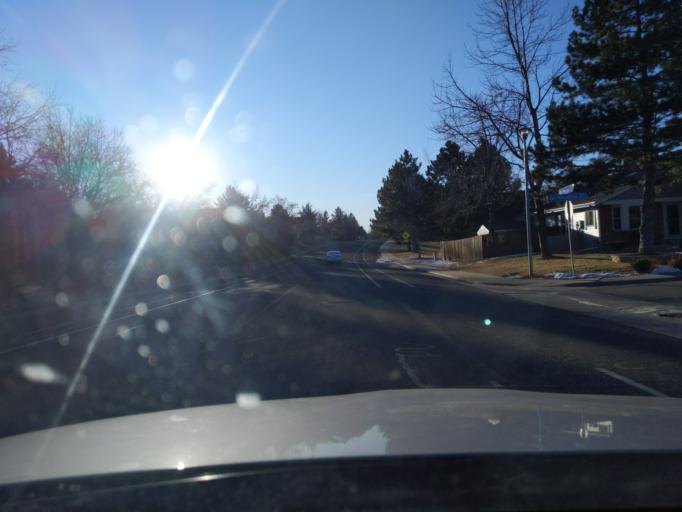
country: US
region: Colorado
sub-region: Arapahoe County
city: Castlewood
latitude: 39.5732
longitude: -104.8919
